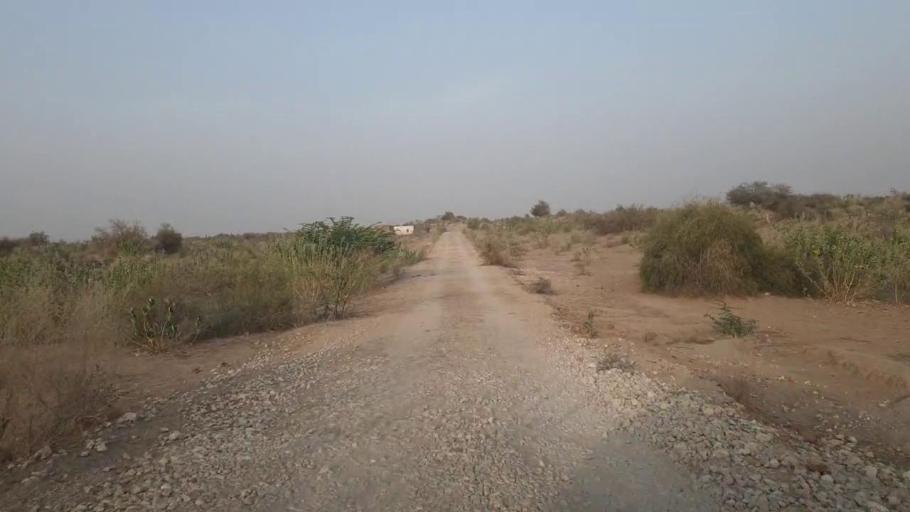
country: PK
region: Sindh
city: Chor
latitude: 25.5249
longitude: 69.9596
